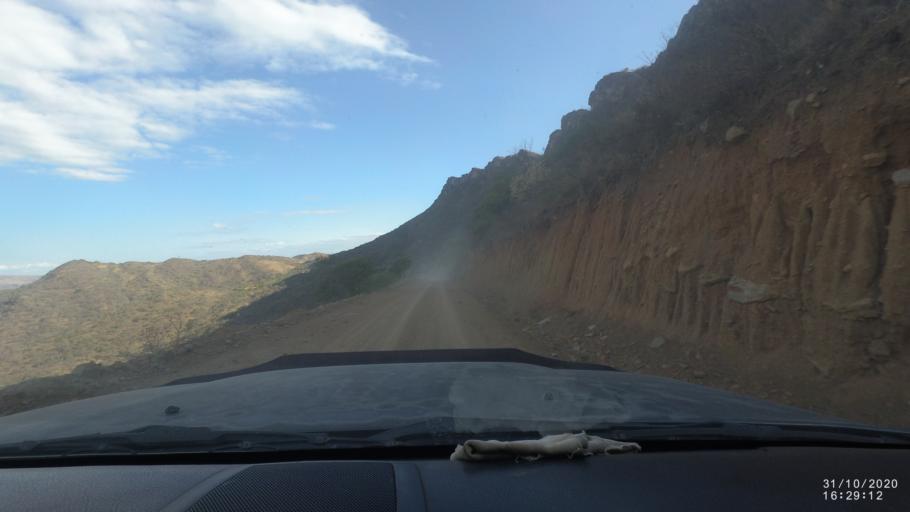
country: BO
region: Chuquisaca
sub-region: Provincia Zudanez
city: Mojocoya
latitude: -18.4182
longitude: -64.5858
